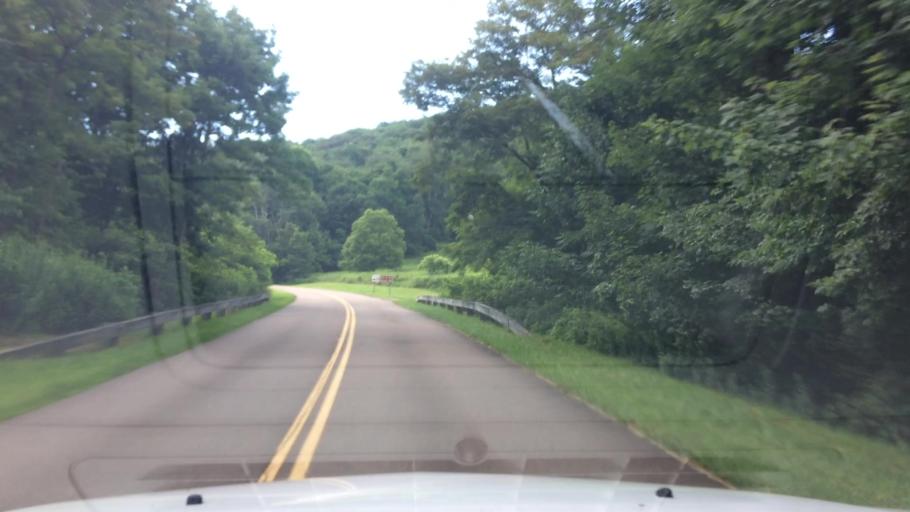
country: US
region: North Carolina
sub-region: Watauga County
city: Blowing Rock
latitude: 36.1563
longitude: -81.6704
